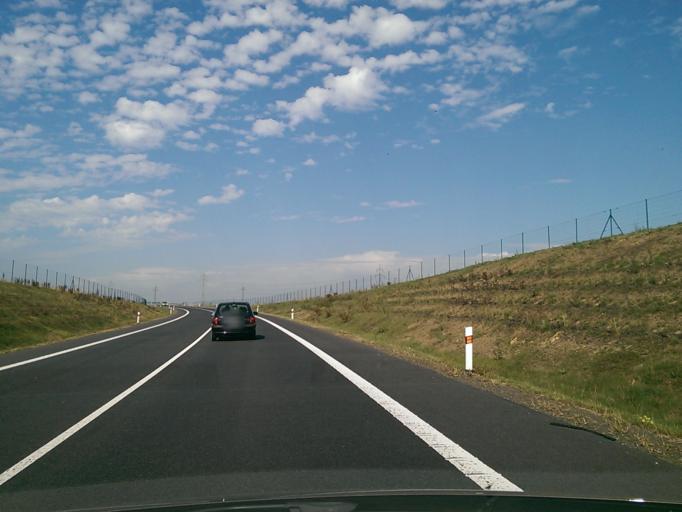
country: CZ
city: Hradek nad Nisou
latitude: 50.8537
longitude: 14.8875
